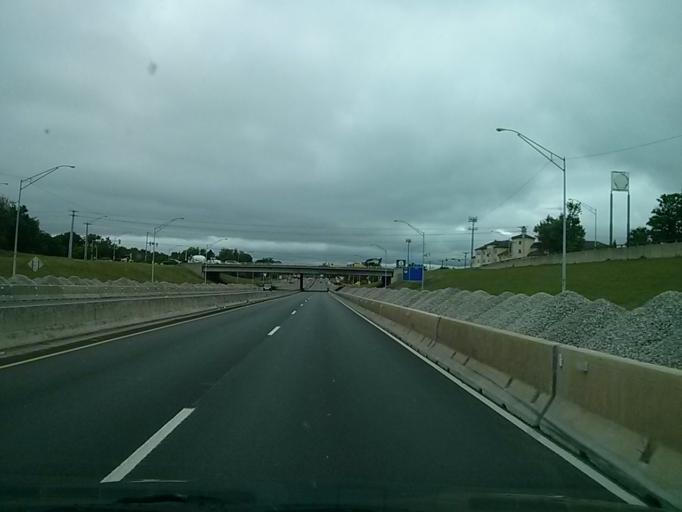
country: US
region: Oklahoma
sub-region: Tulsa County
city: Tulsa
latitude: 36.1592
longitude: -95.9201
